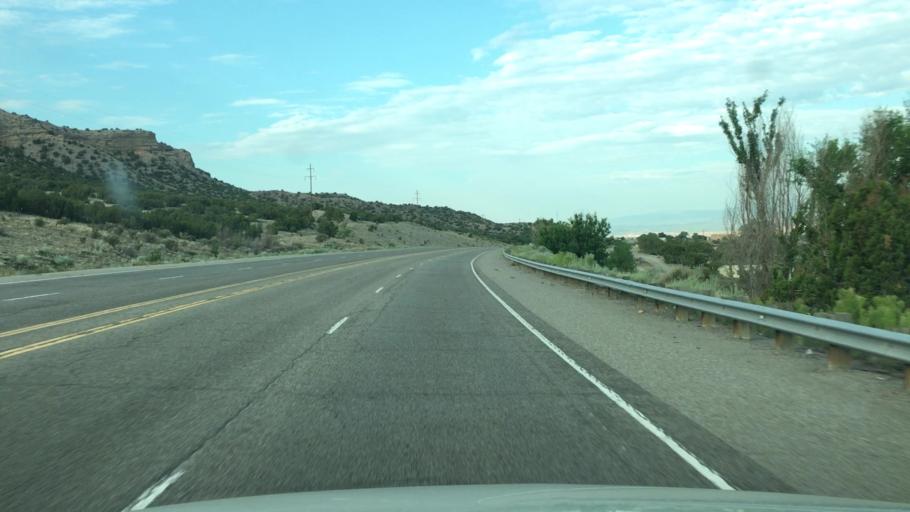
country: US
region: New Mexico
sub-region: Rio Arriba County
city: Ohkay Owingeh
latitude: 36.1544
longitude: -105.9697
